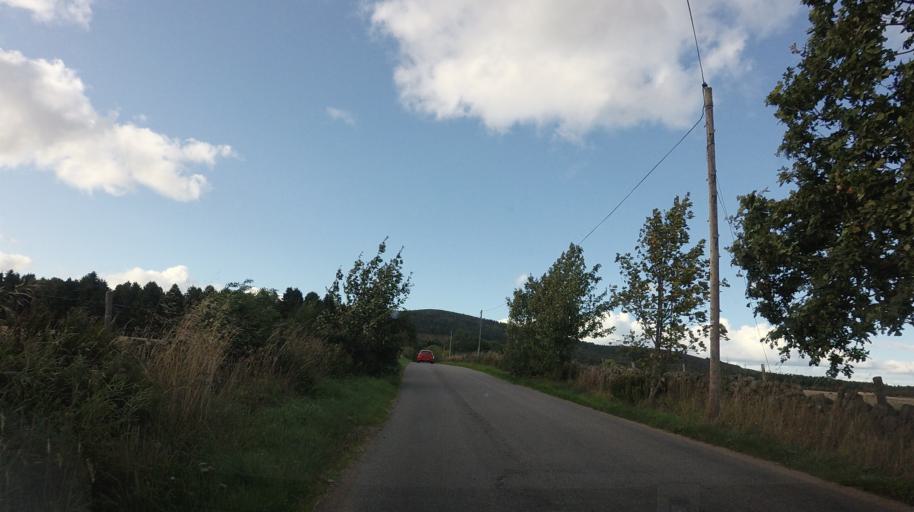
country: GB
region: Scotland
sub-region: Aberdeenshire
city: Banchory
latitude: 57.0943
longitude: -2.4477
